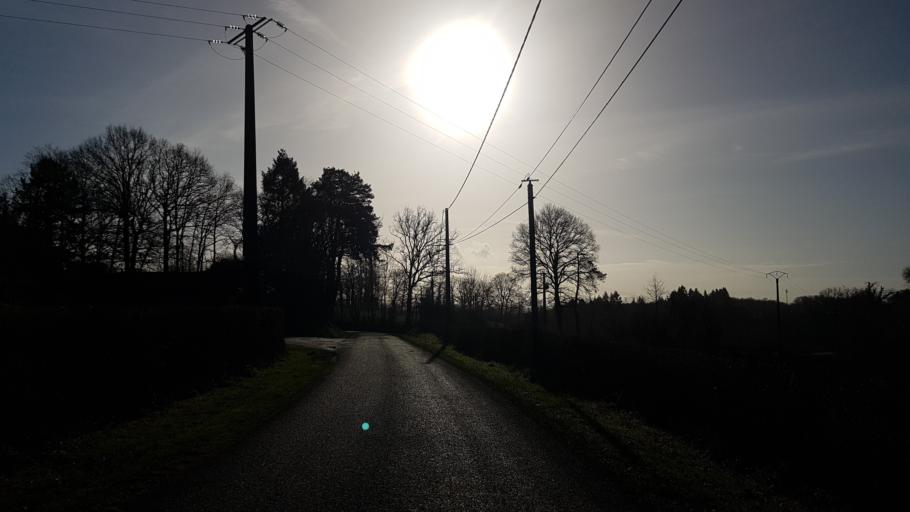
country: FR
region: Poitou-Charentes
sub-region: Departement de la Charente
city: Etagnac
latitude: 45.9024
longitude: 0.8111
